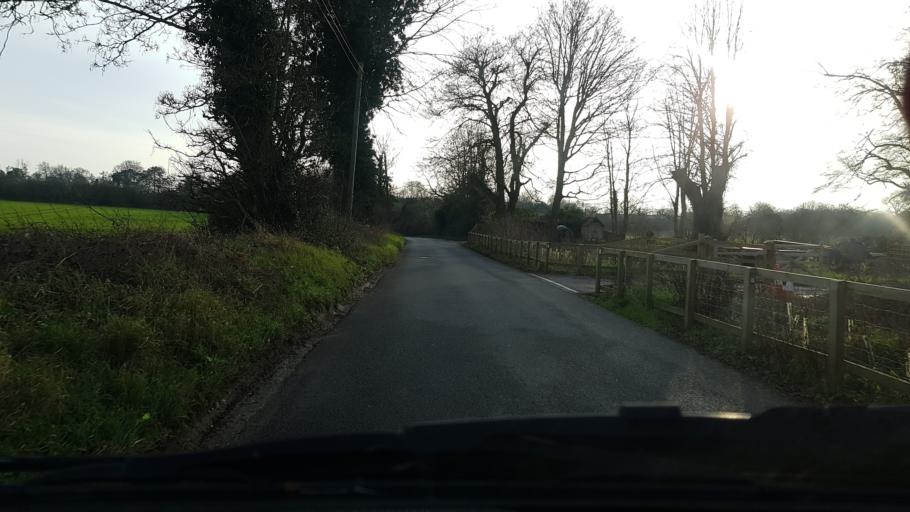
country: GB
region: England
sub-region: Hampshire
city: Abbotts Ann
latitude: 51.2153
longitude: -1.5590
